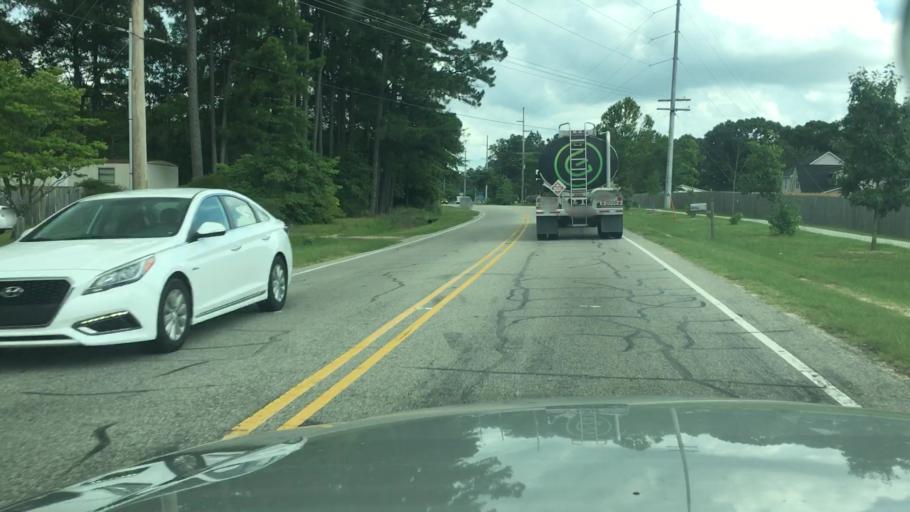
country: US
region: North Carolina
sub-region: Hoke County
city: Rockfish
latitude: 35.0096
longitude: -79.0024
